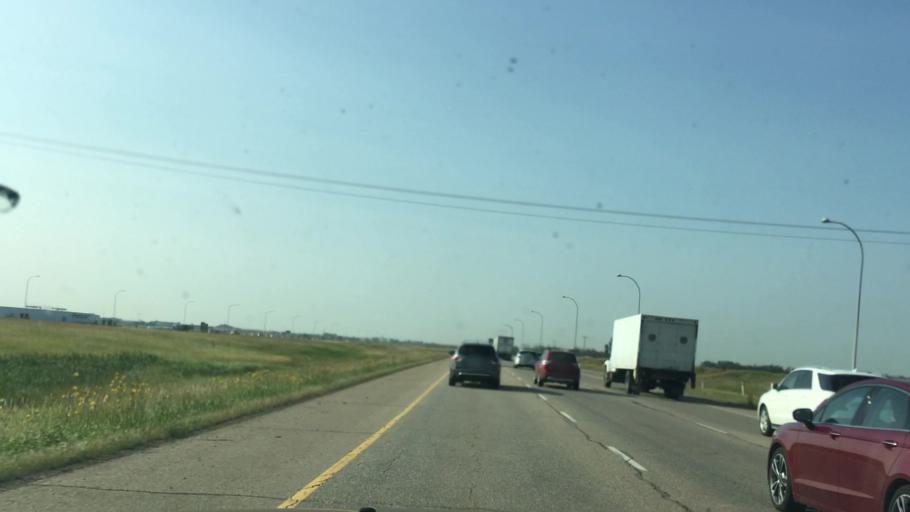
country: CA
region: Alberta
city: Leduc
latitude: 53.3349
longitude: -113.5499
